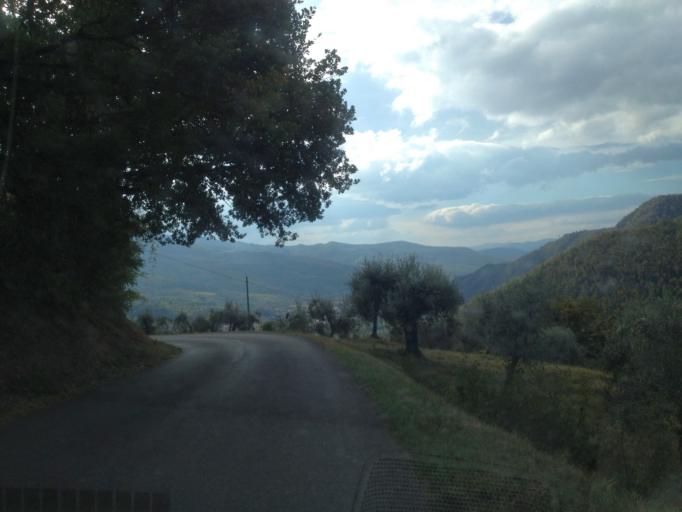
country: IT
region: Tuscany
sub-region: Province of Florence
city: Montebonello
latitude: 43.8587
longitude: 11.4982
